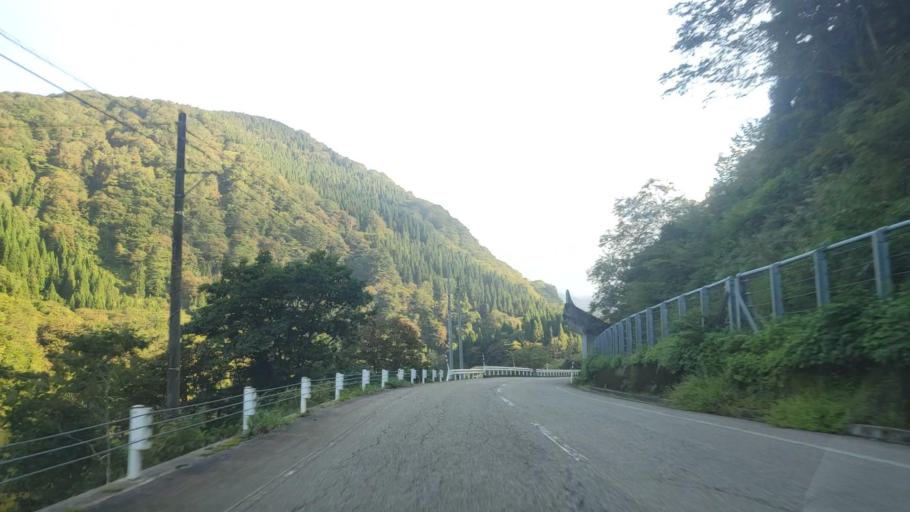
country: JP
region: Toyama
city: Yatsuomachi-higashikumisaka
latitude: 36.4867
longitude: 137.0492
